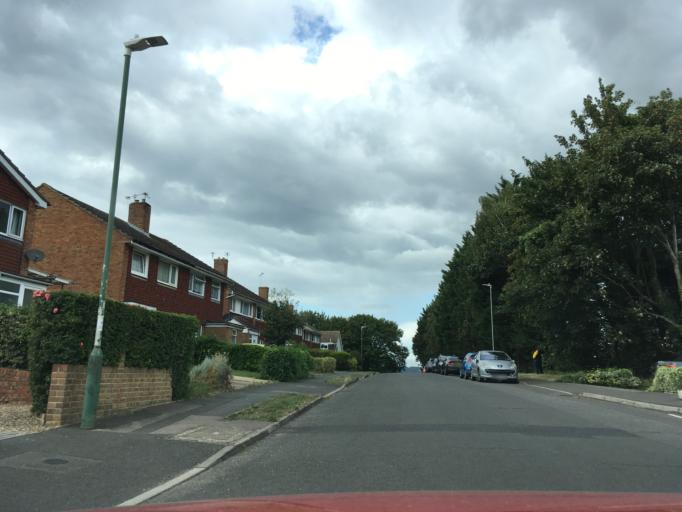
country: GB
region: England
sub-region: Kent
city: Maidstone
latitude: 51.2594
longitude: 0.5229
